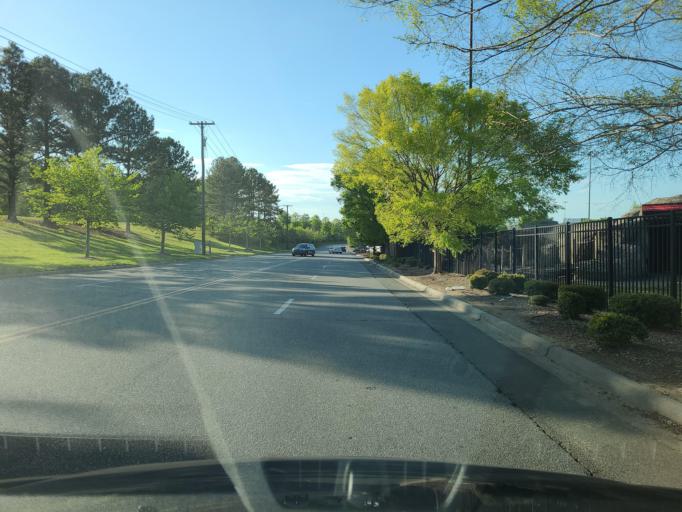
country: US
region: North Carolina
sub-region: Cabarrus County
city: Harrisburg
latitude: 35.3678
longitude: -80.7254
